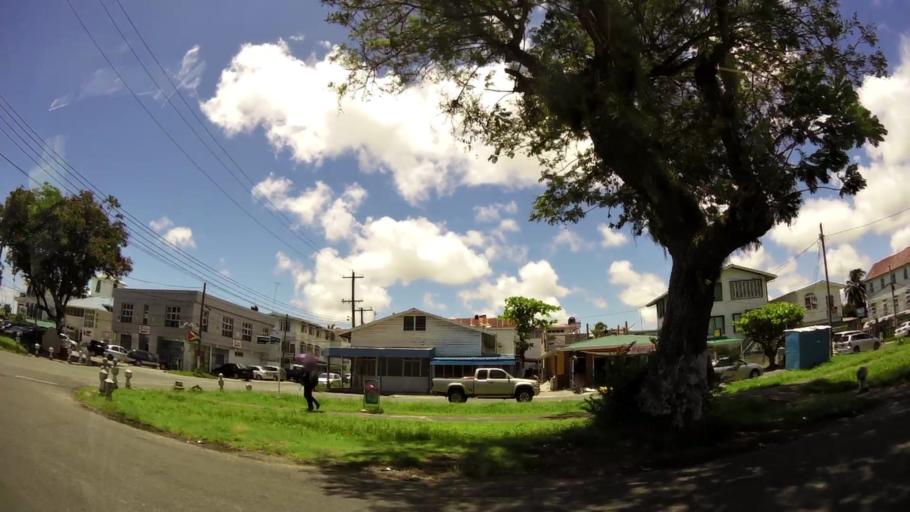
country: GY
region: Demerara-Mahaica
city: Georgetown
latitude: 6.8146
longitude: -58.1633
